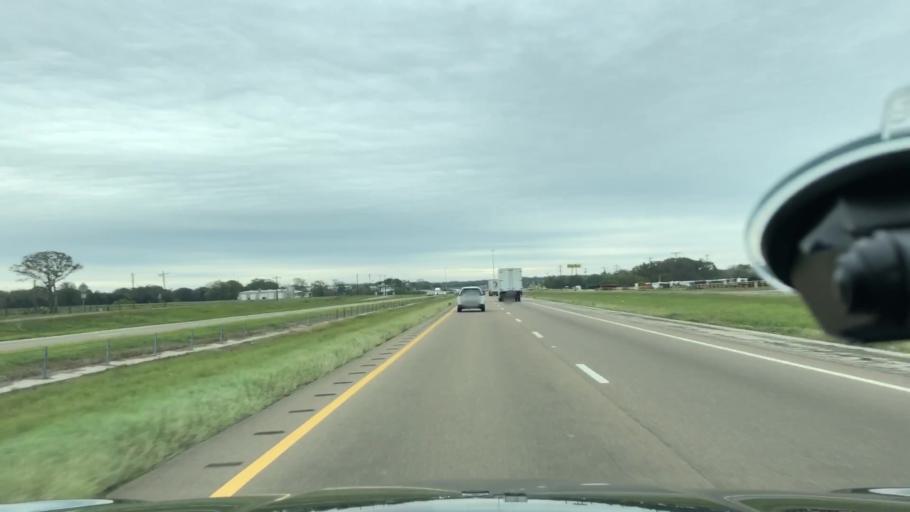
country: US
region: Texas
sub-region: Titus County
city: Mount Pleasant
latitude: 33.1929
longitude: -94.9325
